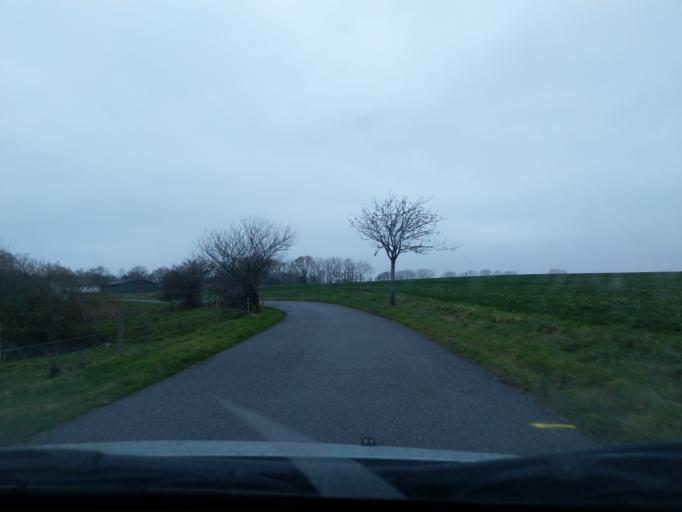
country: DK
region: Zealand
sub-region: Vordingborg Kommune
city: Praesto
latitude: 55.1218
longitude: 12.1314
